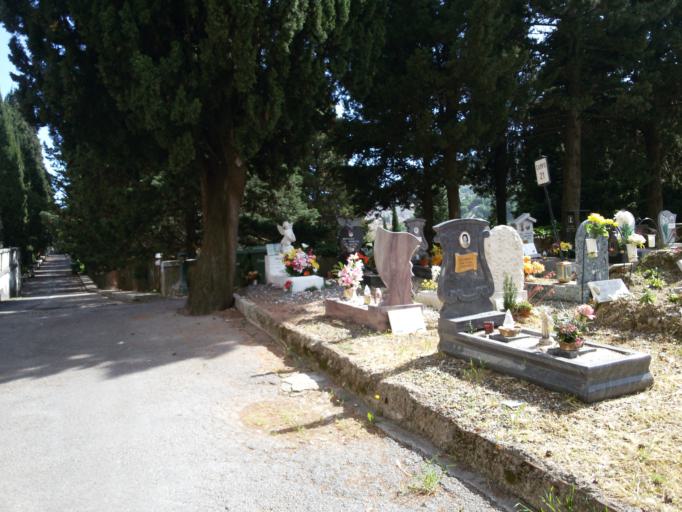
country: IT
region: Liguria
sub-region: Provincia di Genova
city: Genoa
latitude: 44.4327
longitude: 8.9489
